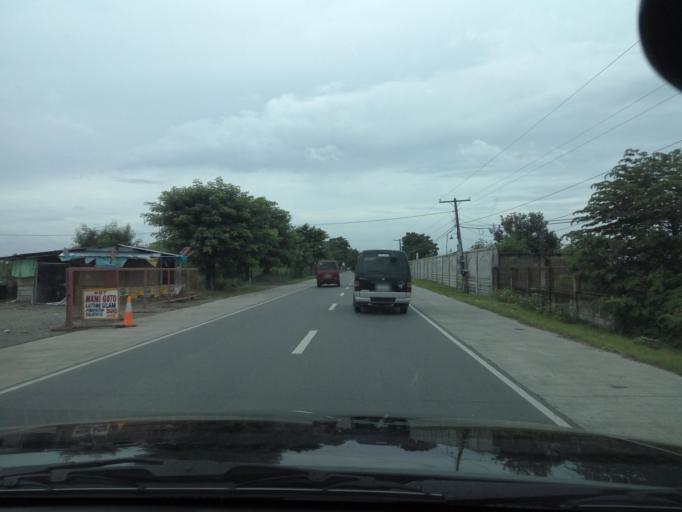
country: PH
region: Central Luzon
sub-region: Province of Nueva Ecija
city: Carmen
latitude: 15.4473
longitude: 120.8157
